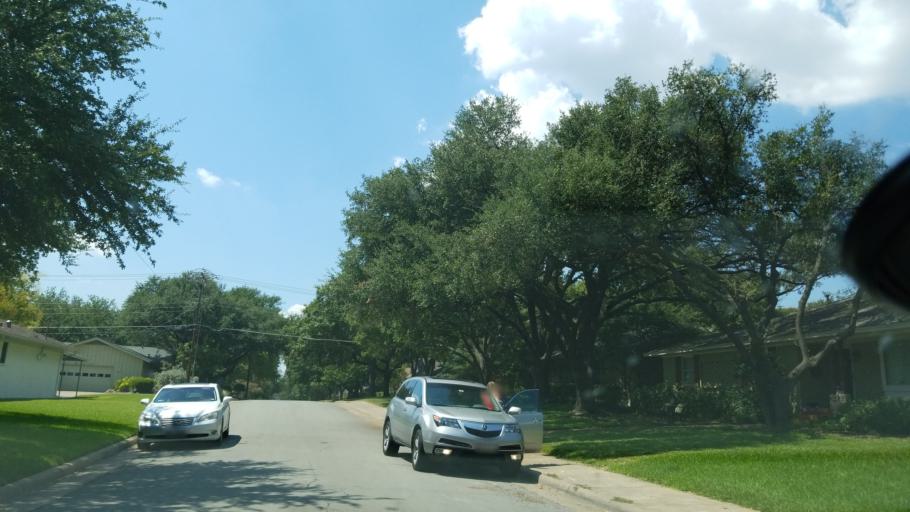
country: US
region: Texas
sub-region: Dallas County
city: Richardson
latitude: 32.8884
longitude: -96.7108
